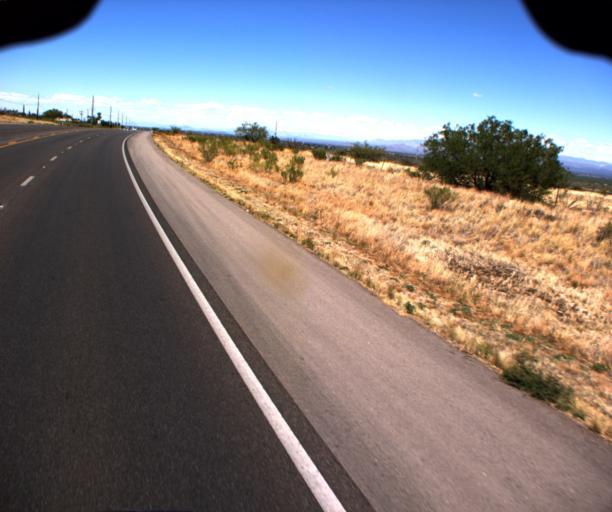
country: US
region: Arizona
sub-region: Cochise County
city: Sierra Vista Southeast
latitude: 31.4484
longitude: -110.2573
